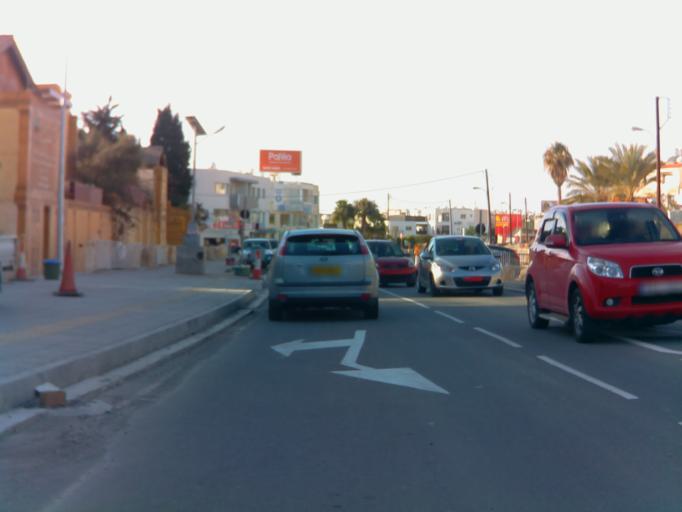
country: CY
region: Pafos
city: Paphos
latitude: 34.7643
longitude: 32.4128
